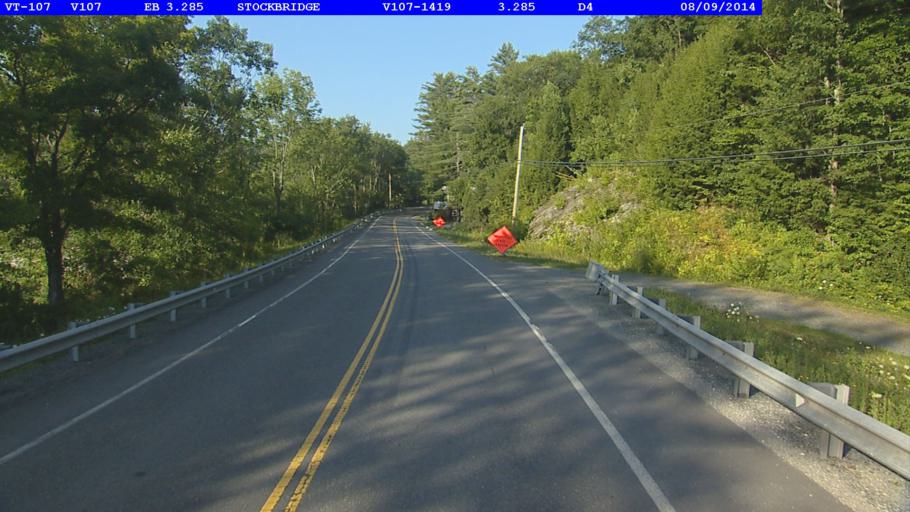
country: US
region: Vermont
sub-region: Orange County
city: Randolph
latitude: 43.7656
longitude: -72.7114
